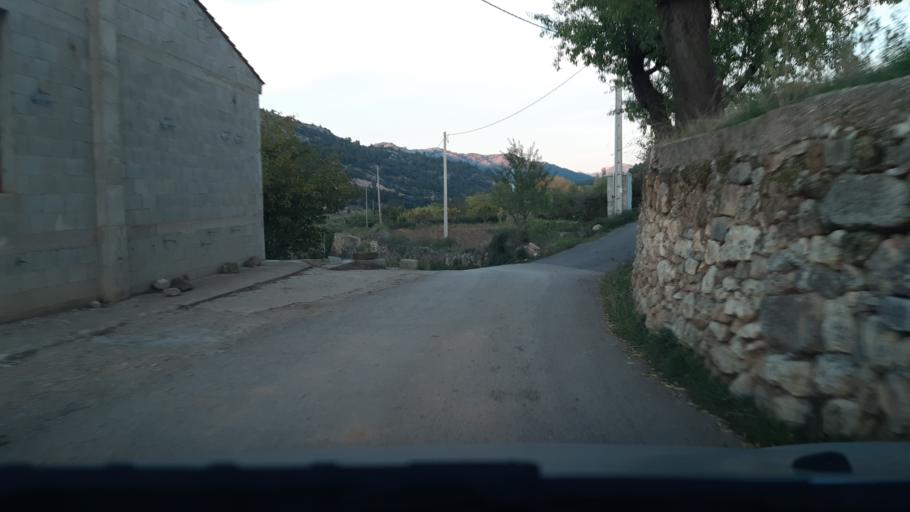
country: ES
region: Aragon
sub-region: Provincia de Teruel
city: Valderrobres
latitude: 40.8363
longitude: 0.1898
